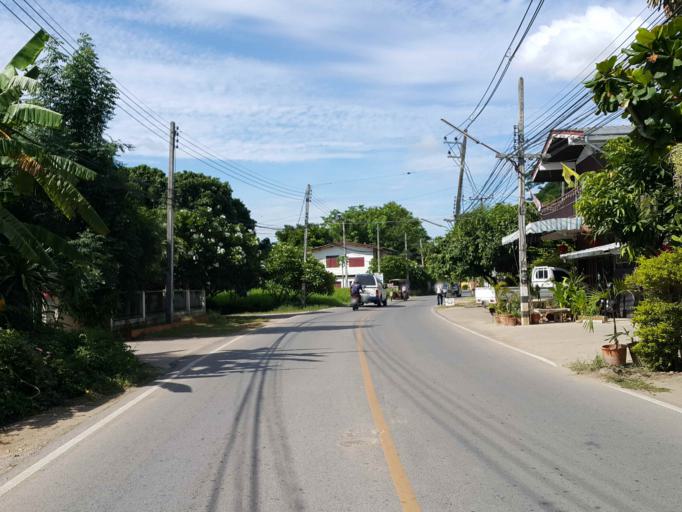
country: TH
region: Chiang Mai
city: Saraphi
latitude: 18.7353
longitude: 98.9897
